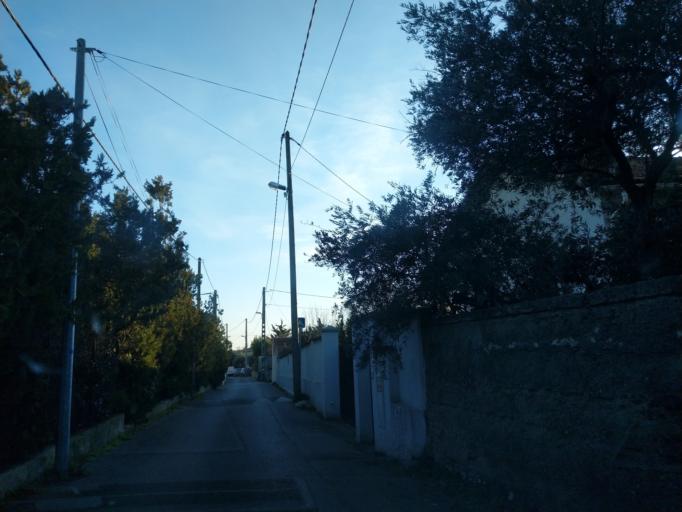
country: FR
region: Provence-Alpes-Cote d'Azur
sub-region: Departement des Bouches-du-Rhone
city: Plan-de-Cuques
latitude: 43.3433
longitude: 5.4514
